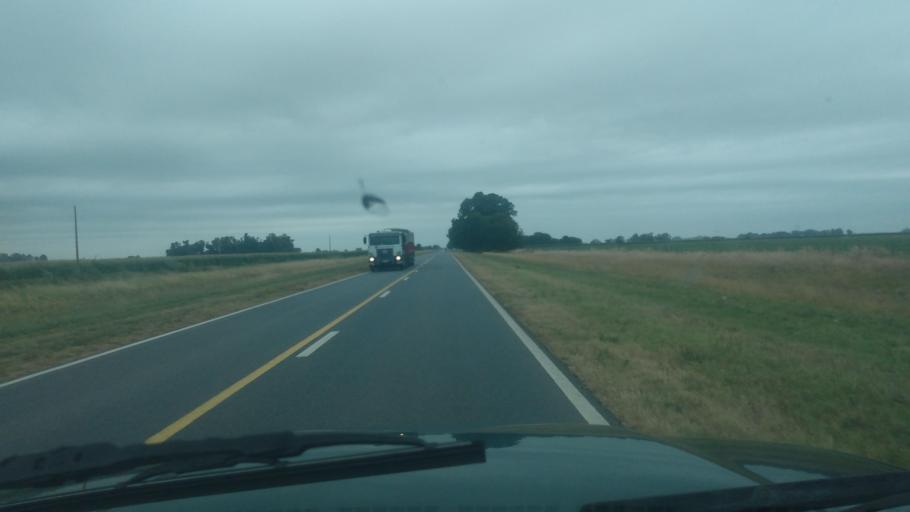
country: AR
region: Buenos Aires
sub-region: Partido de Bragado
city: Bragado
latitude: -35.3045
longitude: -60.6191
